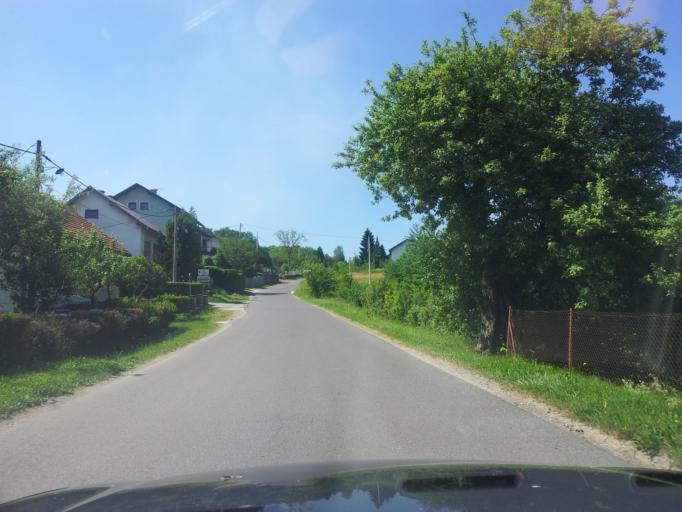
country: HR
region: Karlovacka
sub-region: Grad Karlovac
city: Karlovac
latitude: 45.4924
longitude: 15.5033
